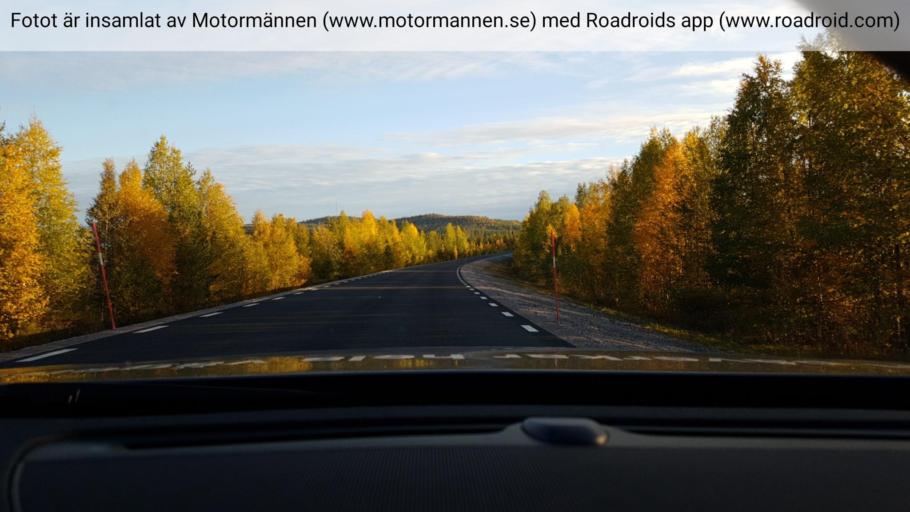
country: SE
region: Norrbotten
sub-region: Jokkmokks Kommun
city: Jokkmokk
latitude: 66.5781
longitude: 19.8056
